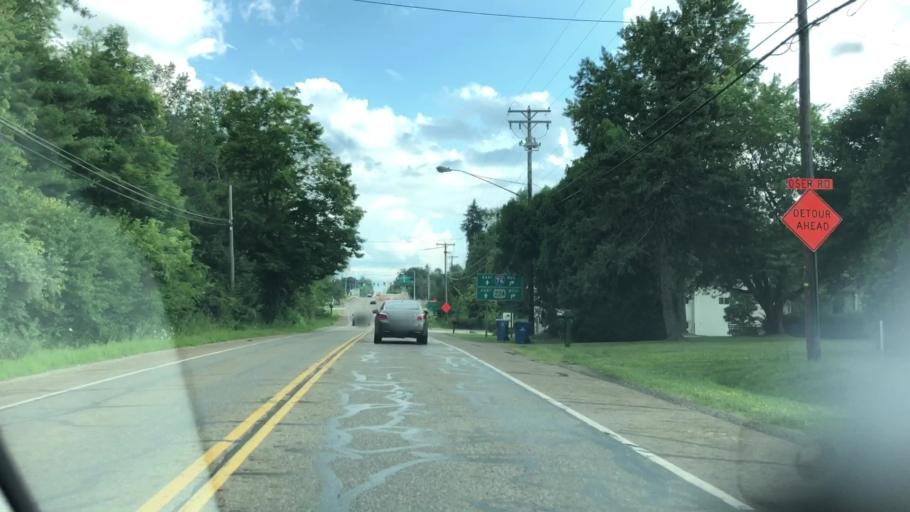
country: US
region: Ohio
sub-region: Summit County
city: Norton
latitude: 41.0428
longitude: -81.6379
